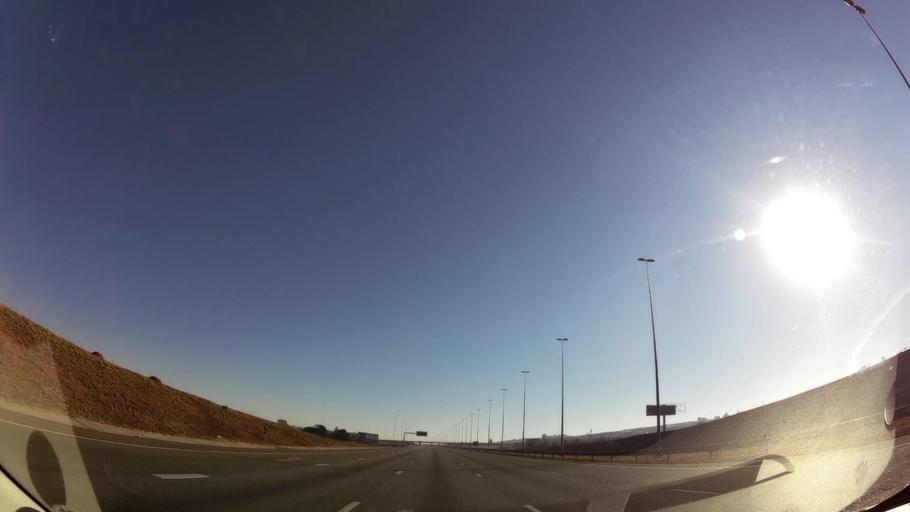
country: ZA
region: Gauteng
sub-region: City of Tshwane Metropolitan Municipality
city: Centurion
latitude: -25.8725
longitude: 28.2543
